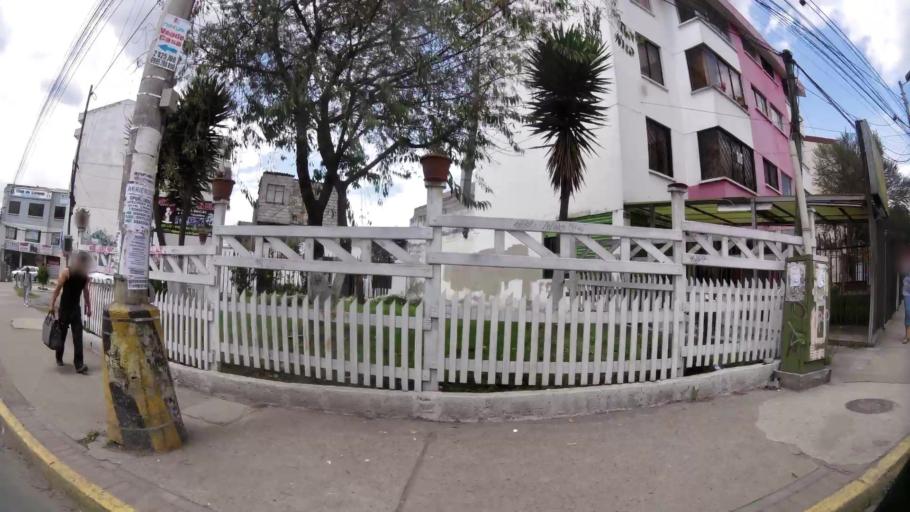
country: EC
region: Pichincha
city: Quito
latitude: -0.1046
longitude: -78.4537
